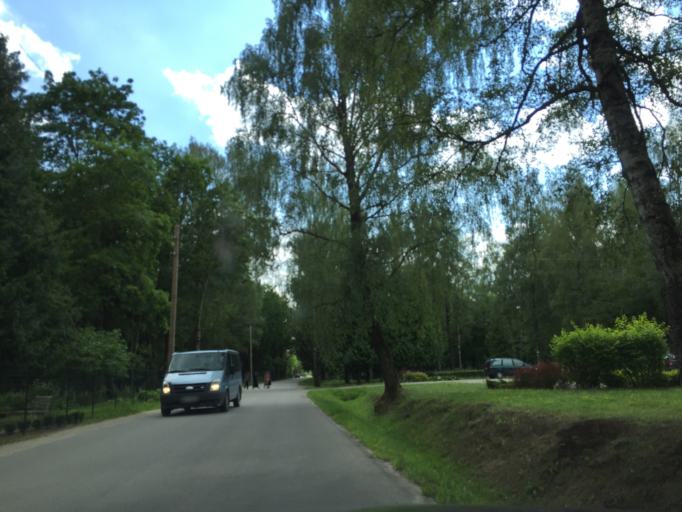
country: LV
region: Jelgava
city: Jelgava
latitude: 56.6265
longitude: 23.6850
